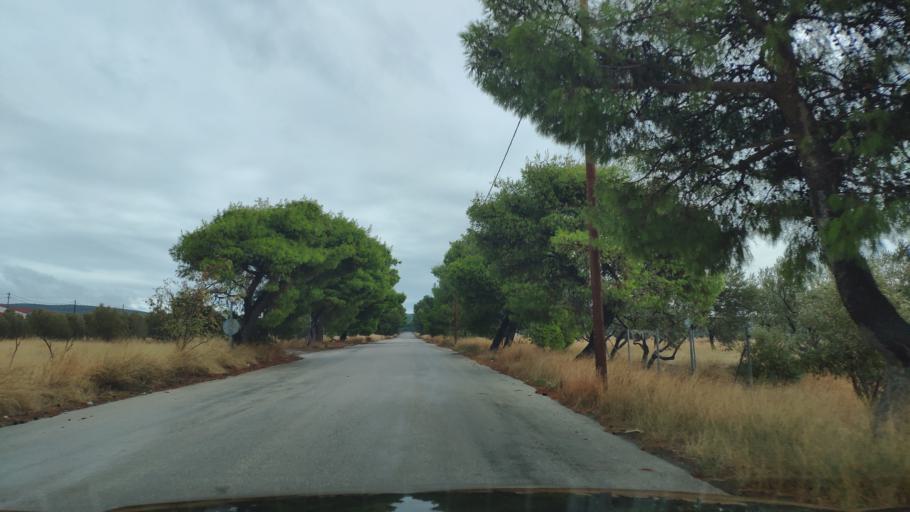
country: GR
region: Peloponnese
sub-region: Nomos Korinthias
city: Loutraki
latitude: 37.9660
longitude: 22.9880
